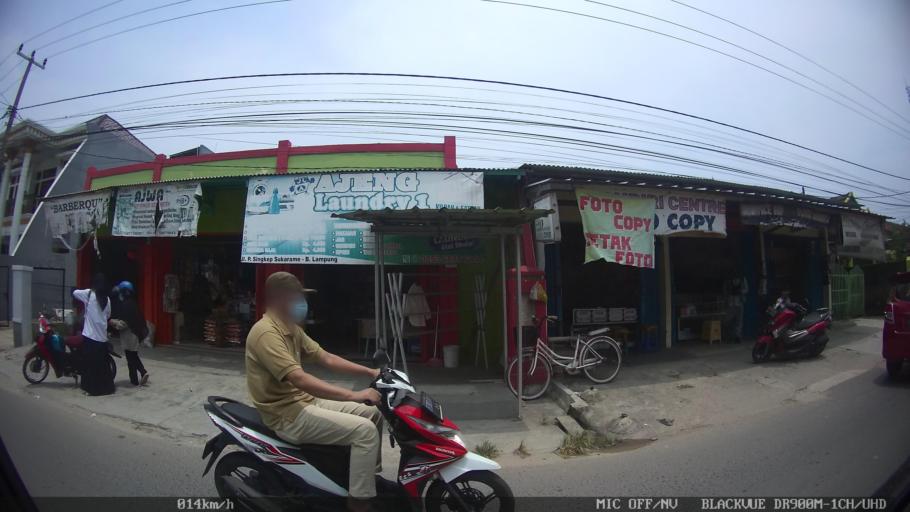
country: ID
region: Lampung
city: Kedaton
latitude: -5.3923
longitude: 105.3000
